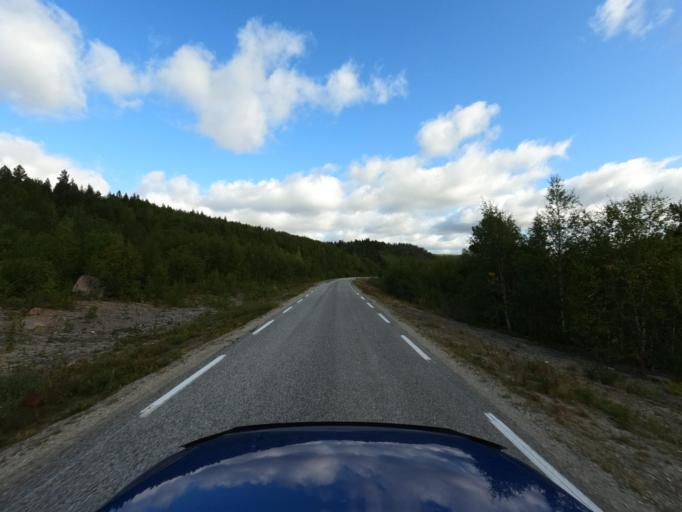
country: NO
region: Finnmark Fylke
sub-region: Porsanger
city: Lakselv
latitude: 69.4242
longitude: 24.8580
